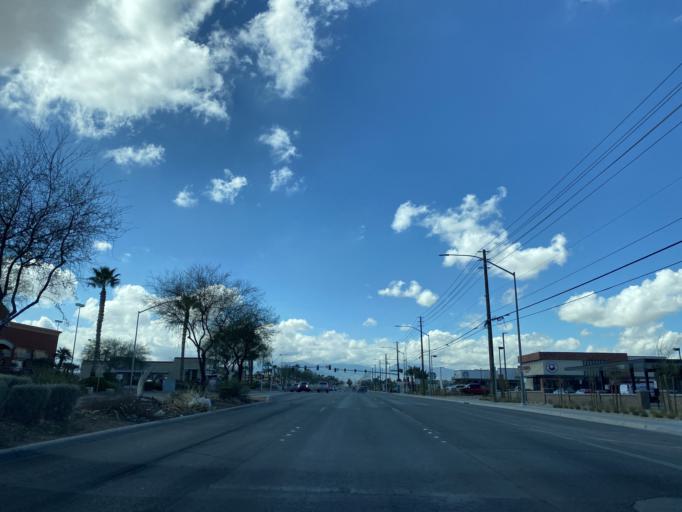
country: US
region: Nevada
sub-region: Clark County
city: North Las Vegas
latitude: 36.2395
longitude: -115.1645
